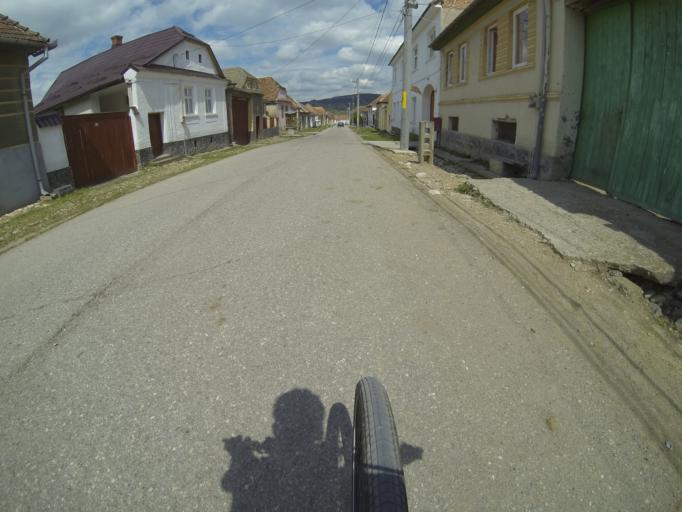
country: RO
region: Brasov
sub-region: Comuna Hoghiz
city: Hoghiz
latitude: 46.0167
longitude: 25.3799
